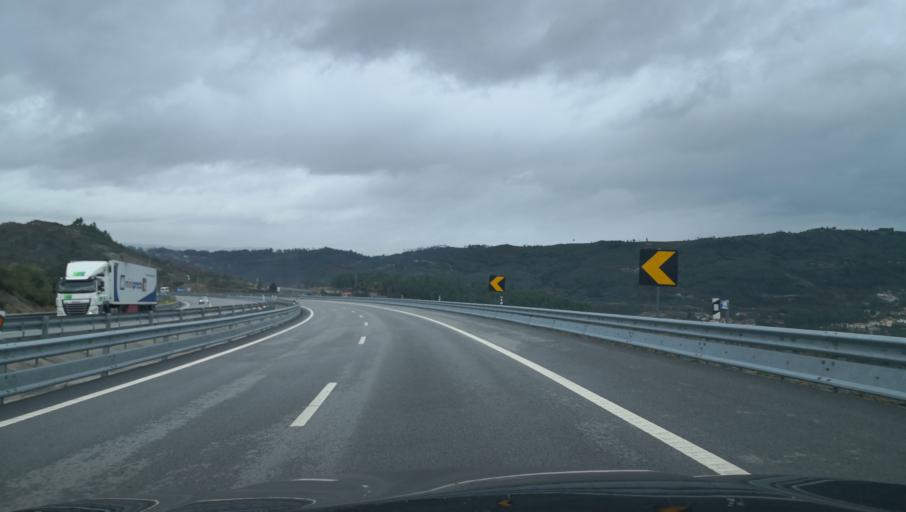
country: PT
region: Porto
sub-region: Amarante
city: Amarante
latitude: 41.2587
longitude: -7.9973
